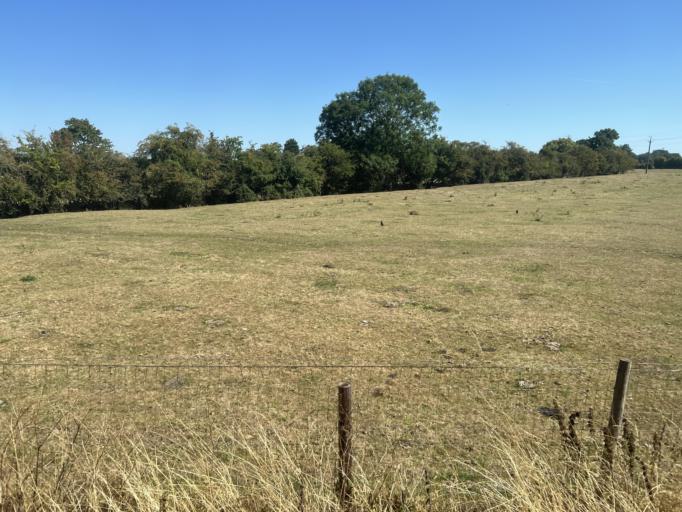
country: GB
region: England
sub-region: Lincolnshire
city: Wainfleet All Saints
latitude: 53.1214
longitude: 0.2016
